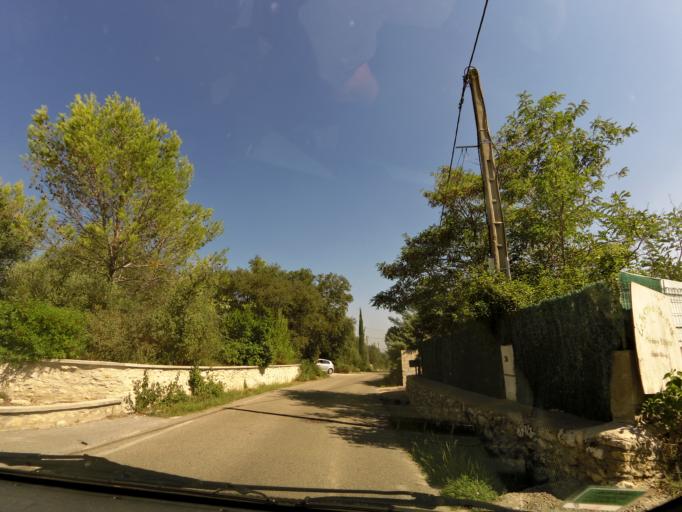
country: FR
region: Languedoc-Roussillon
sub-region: Departement du Gard
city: Villevieille
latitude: 43.7952
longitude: 4.1008
